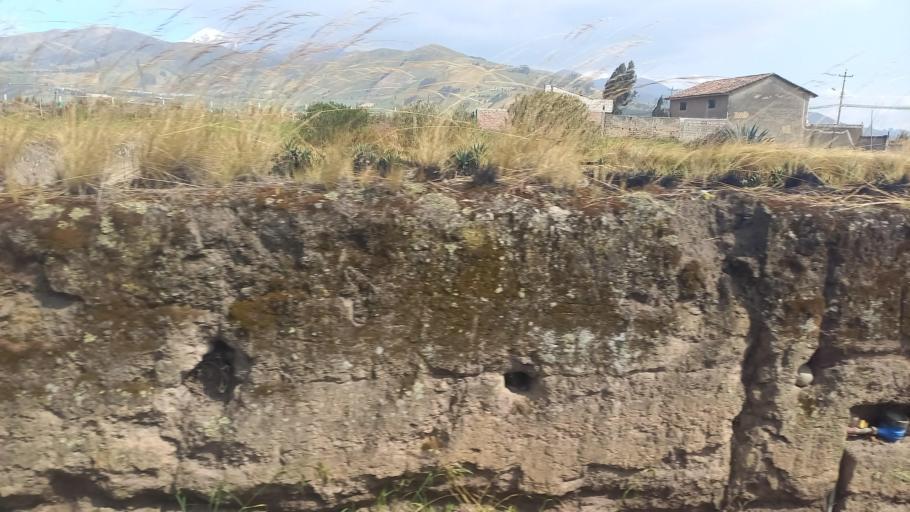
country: EC
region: Pichincha
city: Cayambe
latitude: 0.1413
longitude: -78.0737
